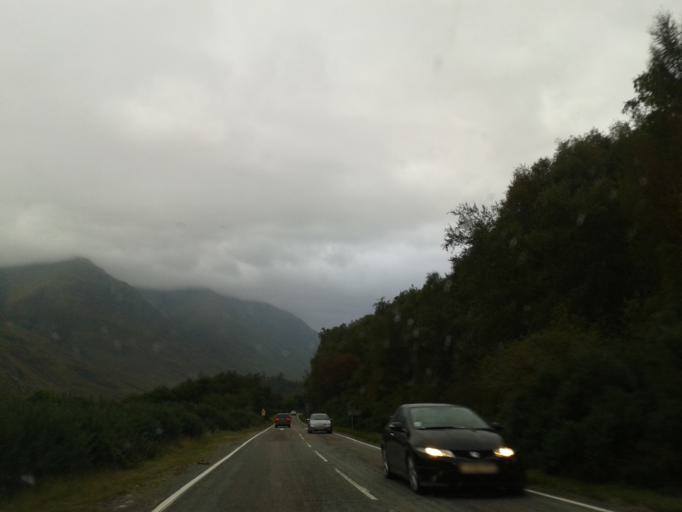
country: GB
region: Scotland
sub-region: Highland
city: Fort William
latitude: 57.2120
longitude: -5.4130
